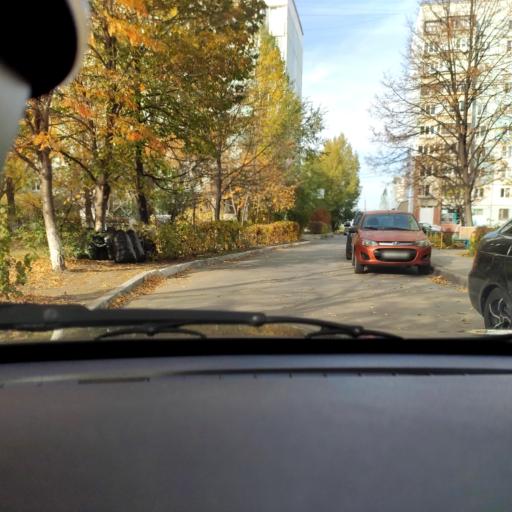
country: RU
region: Samara
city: Tol'yatti
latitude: 53.5470
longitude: 49.3413
